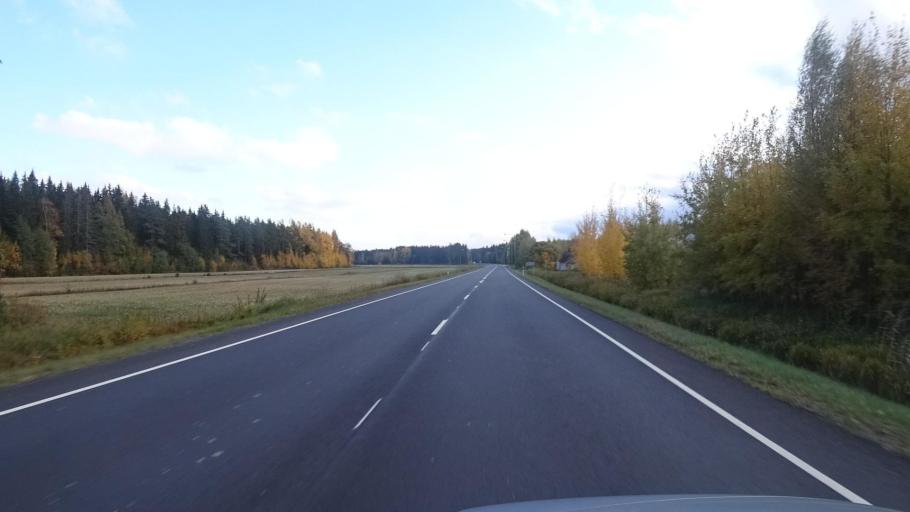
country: FI
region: Satakunta
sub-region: Rauma
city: Koeylioe
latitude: 61.0993
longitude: 22.2361
